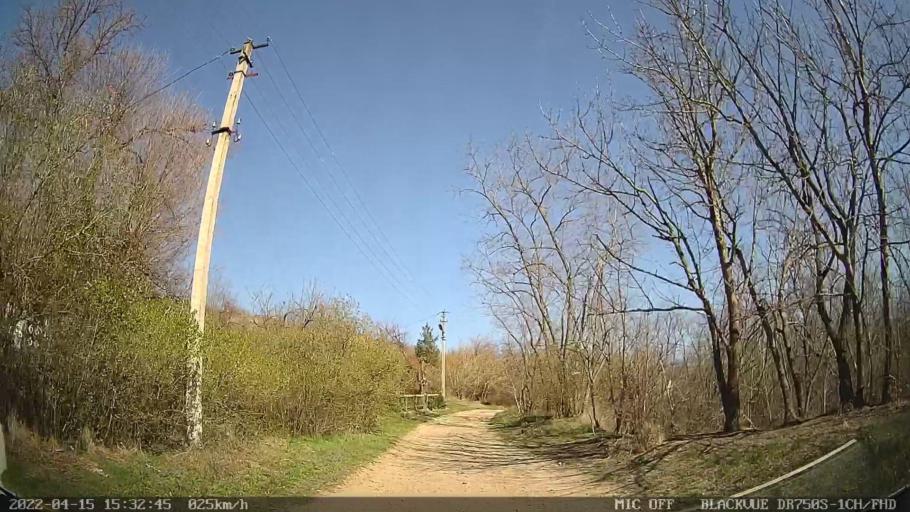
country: MD
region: Raionul Ocnita
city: Otaci
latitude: 48.3507
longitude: 27.9217
